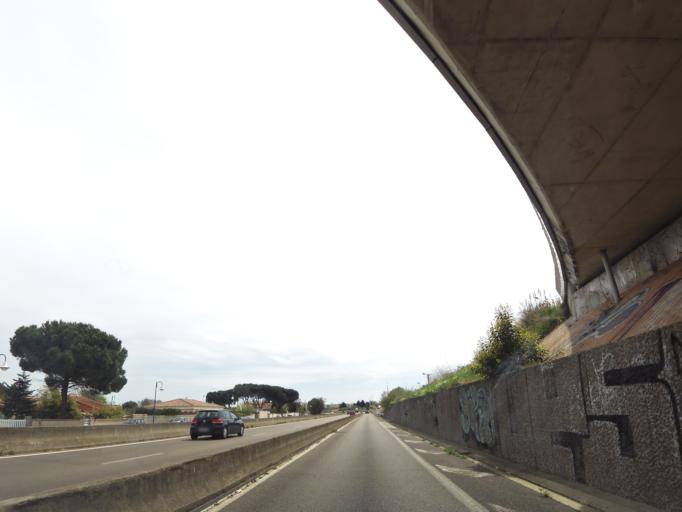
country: FR
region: Languedoc-Roussillon
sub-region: Departement de l'Herault
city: Perols
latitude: 43.5546
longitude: 3.9670
